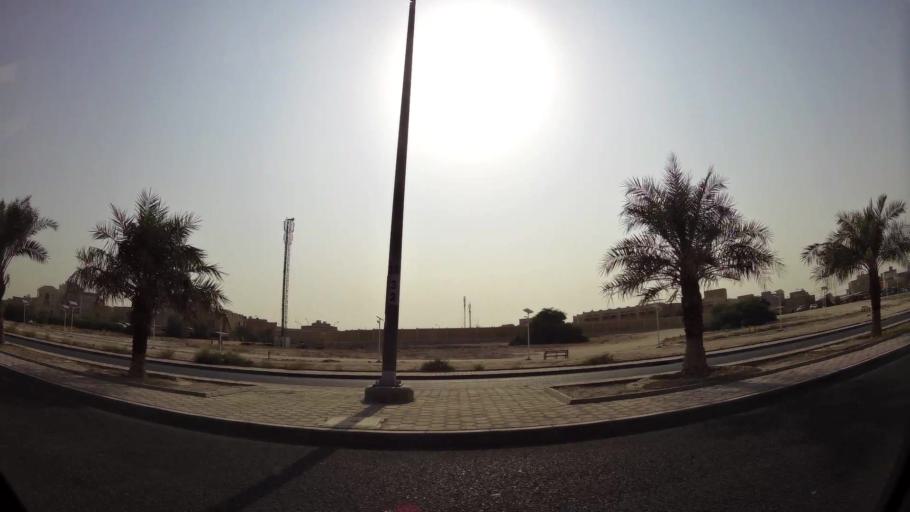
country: KW
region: Al Asimah
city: Ar Rabiyah
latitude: 29.3005
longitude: 47.8579
